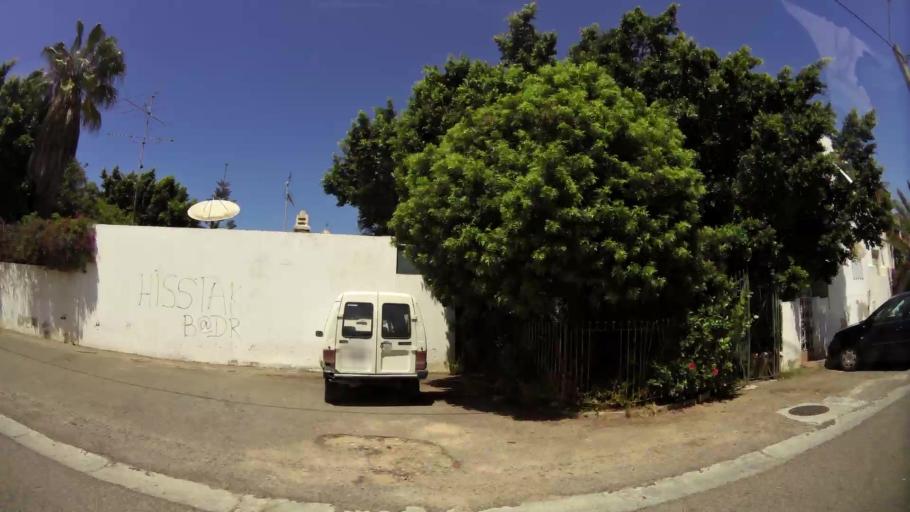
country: MA
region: Souss-Massa-Draa
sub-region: Agadir-Ida-ou-Tnan
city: Agadir
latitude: 30.4307
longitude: -9.5960
